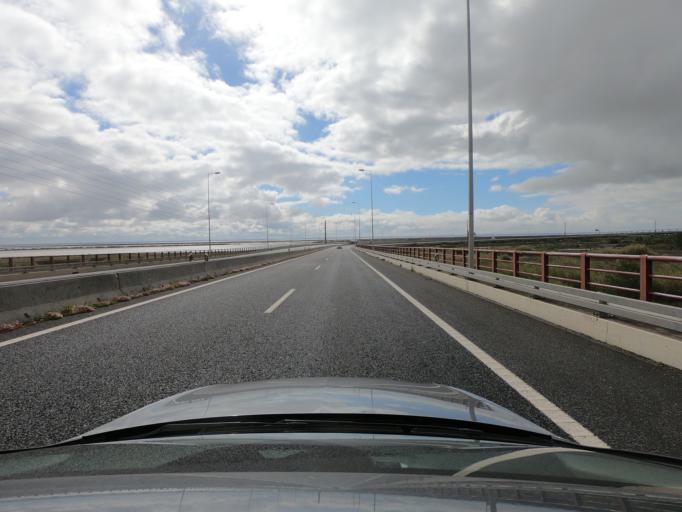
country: PT
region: Lisbon
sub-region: Loures
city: Santa Iria da Azoia
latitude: 38.8441
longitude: -9.0760
